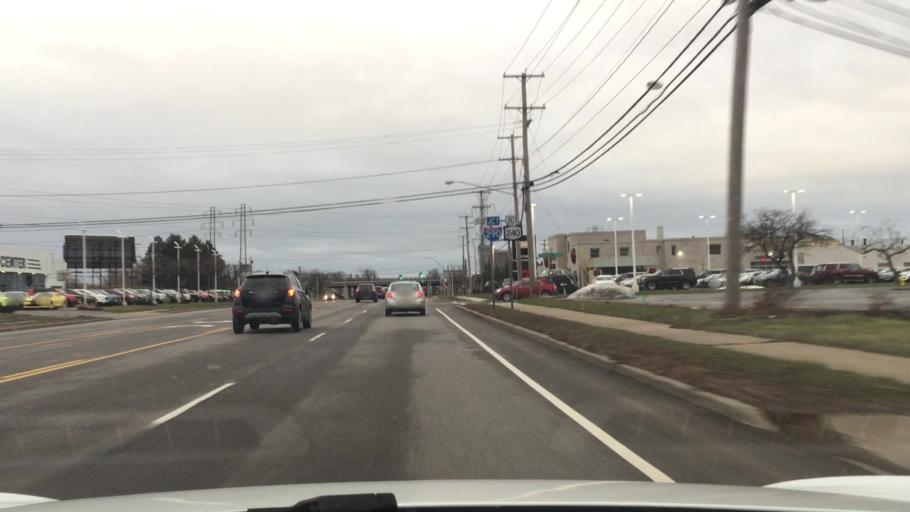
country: US
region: New York
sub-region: Erie County
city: Amherst
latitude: 42.9784
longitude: -78.7789
